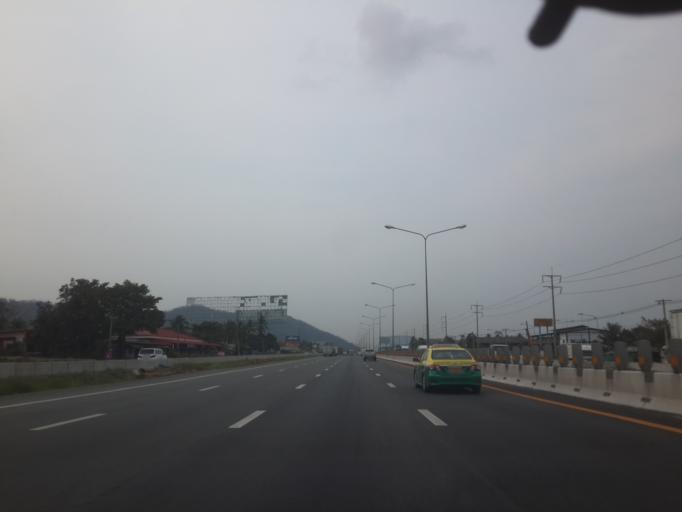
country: TH
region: Chon Buri
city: Si Racha
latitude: 13.2422
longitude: 100.9962
